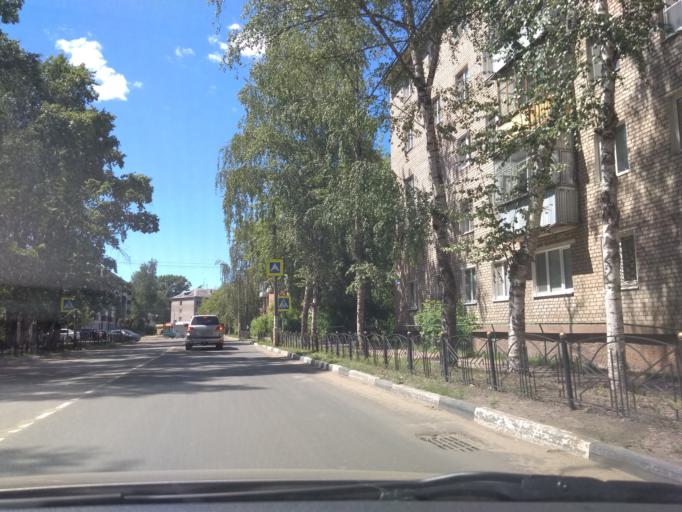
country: RU
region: Moskovskaya
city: Orekhovo-Zuyevo
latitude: 55.8099
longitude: 38.9940
